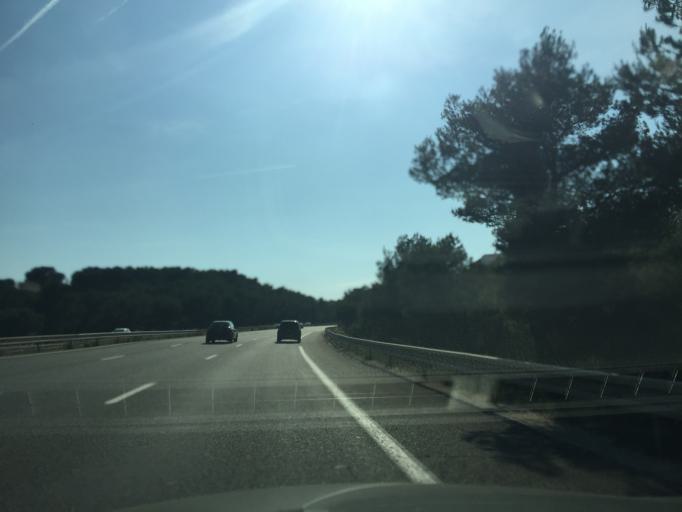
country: FR
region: Provence-Alpes-Cote d'Azur
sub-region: Departement des Bouches-du-Rhone
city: Martigues
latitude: 43.3943
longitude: 5.0648
